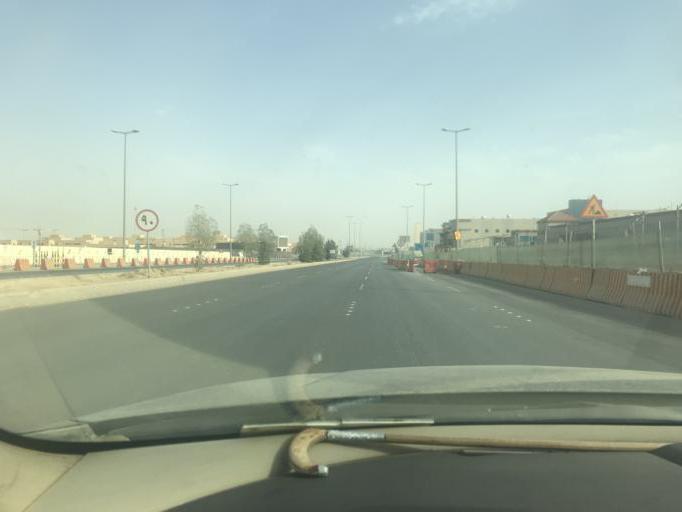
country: SA
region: Ar Riyad
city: Riyadh
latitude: 24.8205
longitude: 46.6864
